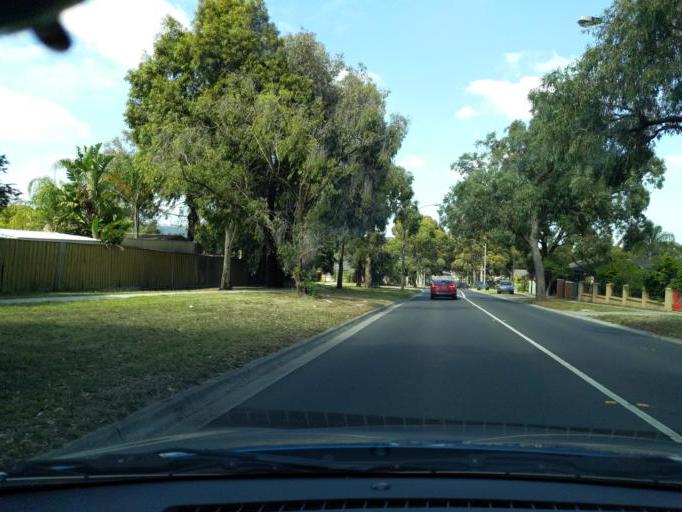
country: AU
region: Victoria
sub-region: Knox
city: Scoresby
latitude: -37.9136
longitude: 145.2467
